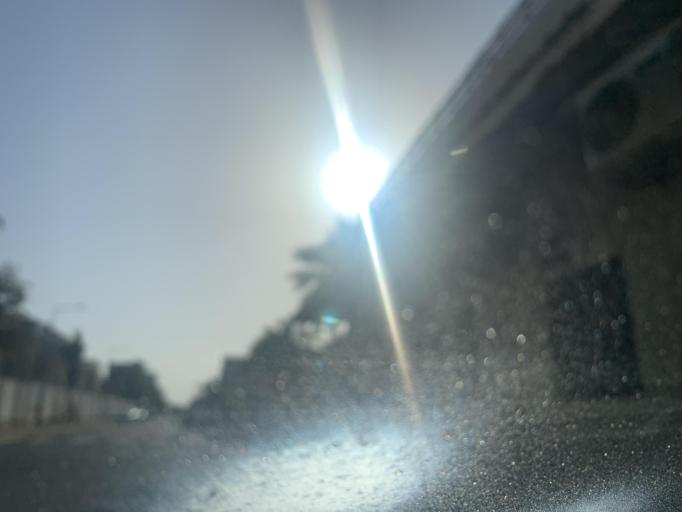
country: BH
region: Manama
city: Jidd Hafs
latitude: 26.2102
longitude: 50.4492
